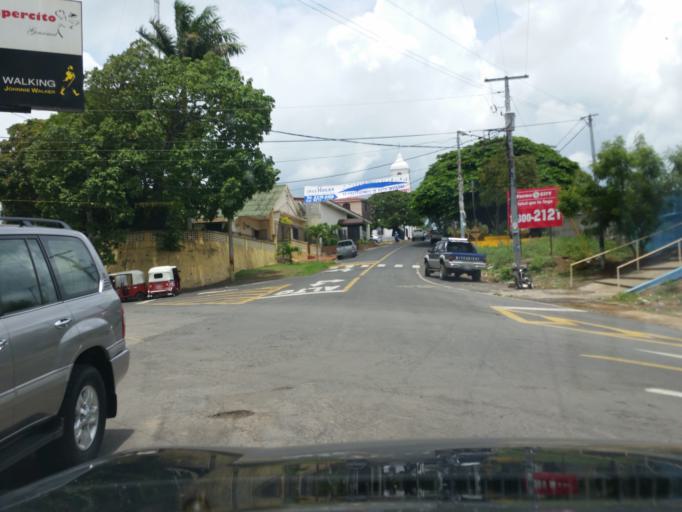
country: NI
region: Managua
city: Managua
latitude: 12.0856
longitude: -86.2406
